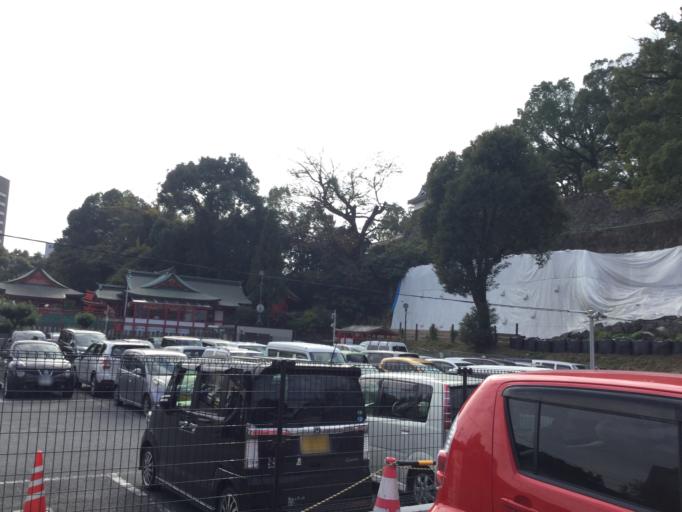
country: JP
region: Kumamoto
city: Kumamoto
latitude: 32.8056
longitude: 130.7080
